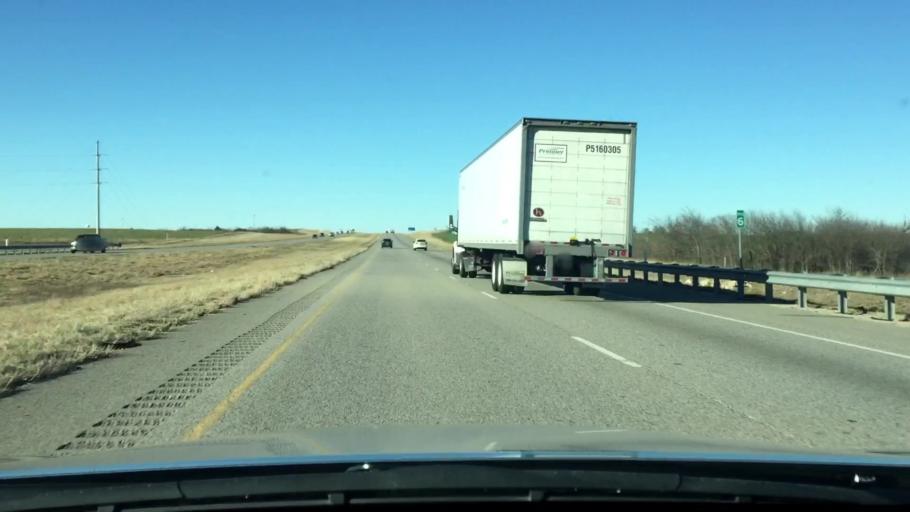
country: US
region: Texas
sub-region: Hill County
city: Itasca
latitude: 32.1347
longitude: -97.1205
